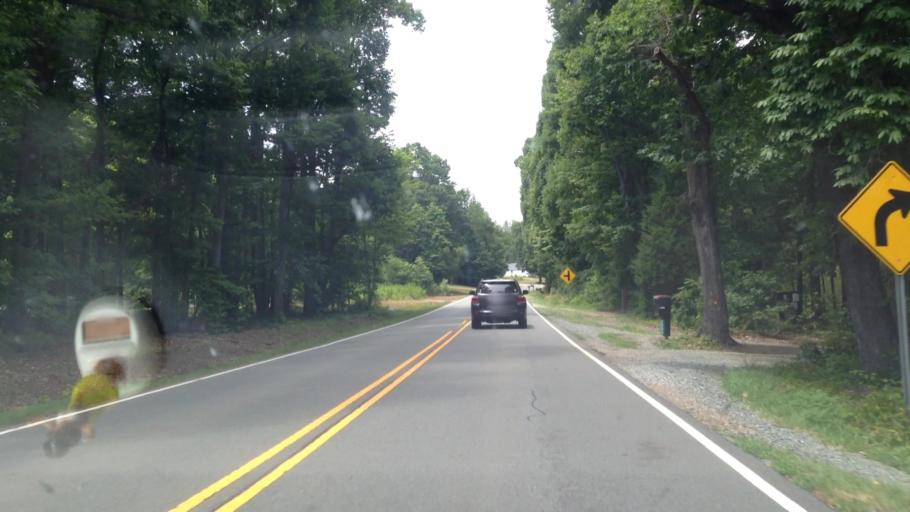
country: US
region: North Carolina
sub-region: Stokes County
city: Walnut Cove
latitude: 36.3808
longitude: -80.0936
